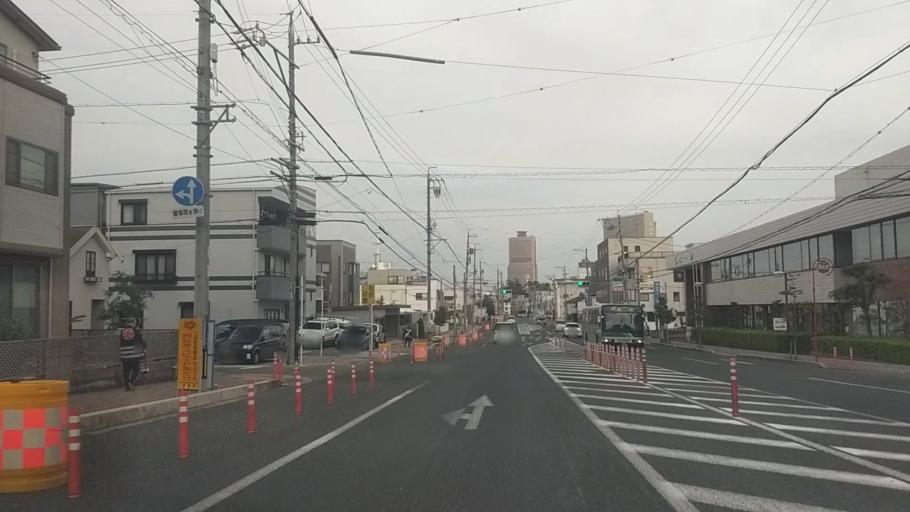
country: JP
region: Shizuoka
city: Hamamatsu
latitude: 34.7180
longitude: 137.7234
